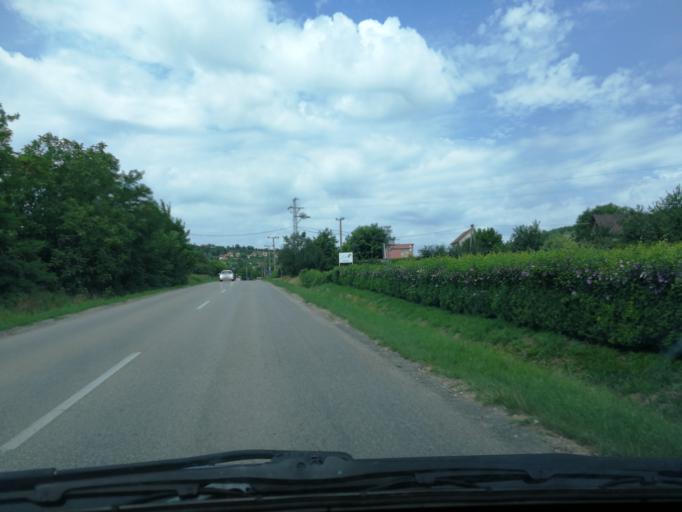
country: HU
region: Baranya
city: Harkany
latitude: 45.8788
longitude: 18.2413
